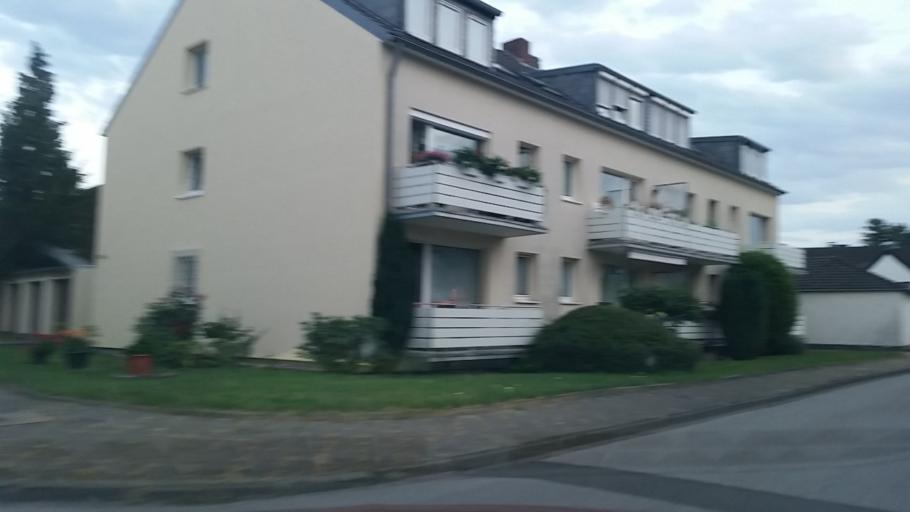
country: DE
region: North Rhine-Westphalia
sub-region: Regierungsbezirk Dusseldorf
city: Meerbusch
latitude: 51.2435
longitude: 6.6903
